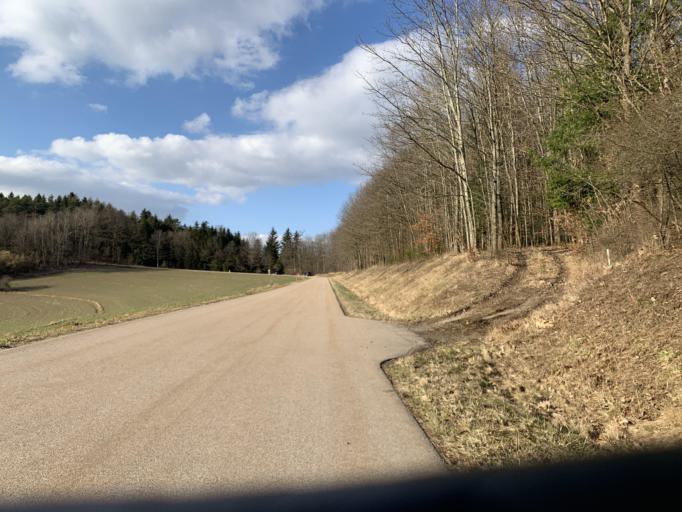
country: DE
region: Bavaria
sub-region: Upper Palatinate
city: Thanstein
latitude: 49.3819
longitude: 12.4580
